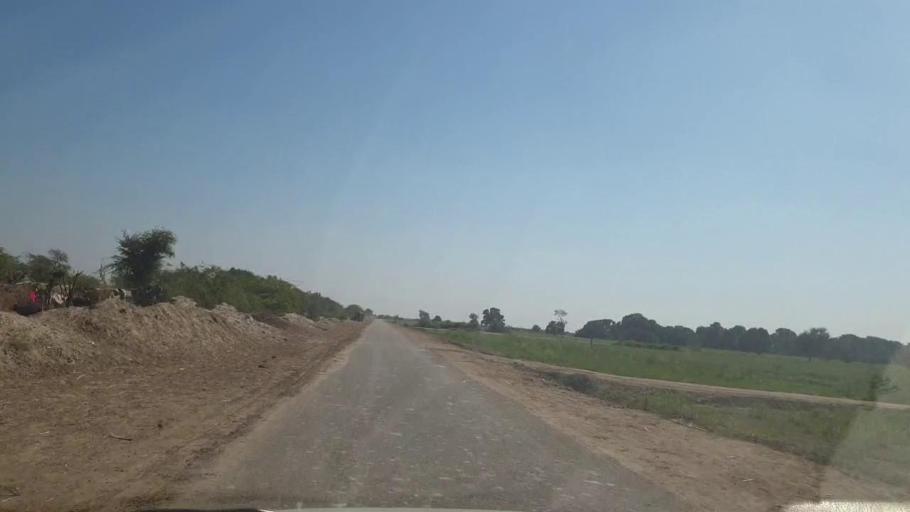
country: PK
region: Sindh
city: Mirpur Khas
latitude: 25.4640
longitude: 69.1796
